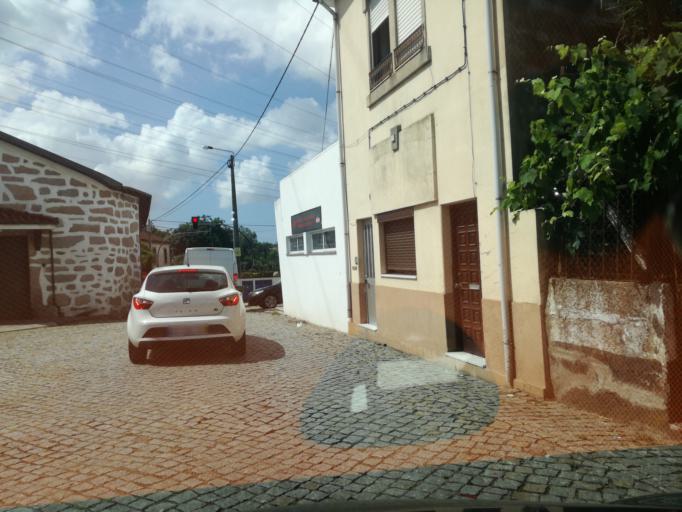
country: PT
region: Porto
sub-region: Maia
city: Nogueira
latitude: 41.2348
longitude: -8.5951
